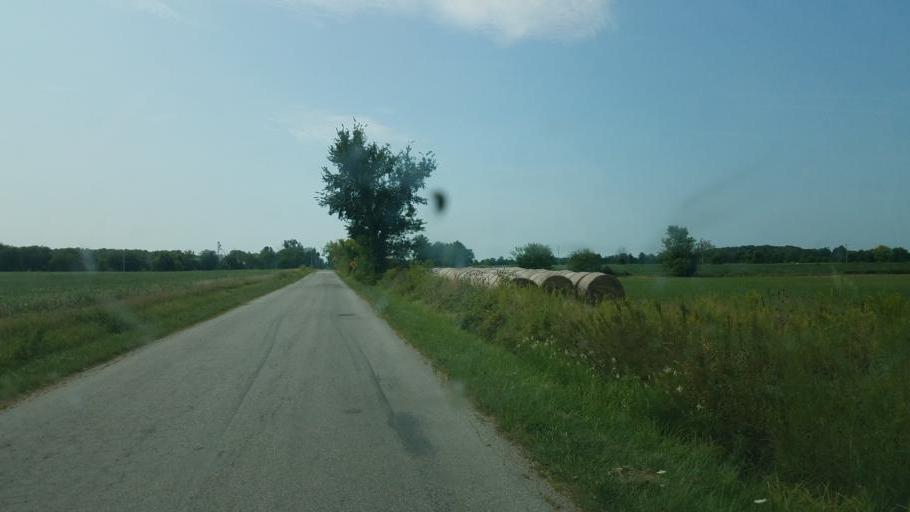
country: US
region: Ohio
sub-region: Delaware County
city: Ashley
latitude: 40.4589
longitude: -83.0088
